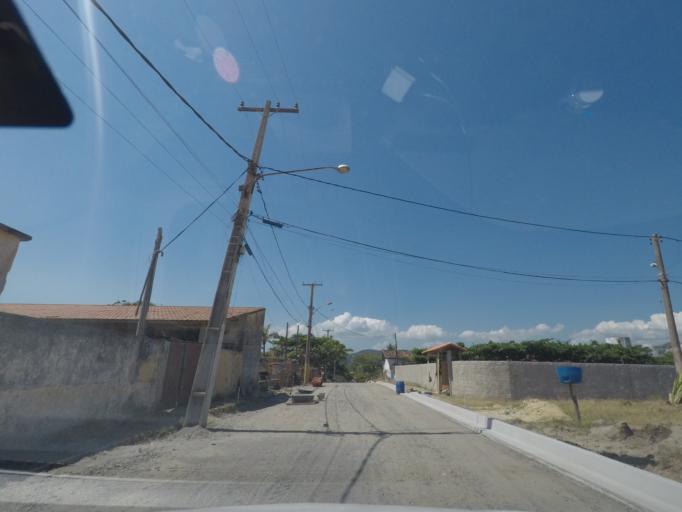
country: BR
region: Rio de Janeiro
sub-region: Marica
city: Marica
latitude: -22.9716
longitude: -42.9055
